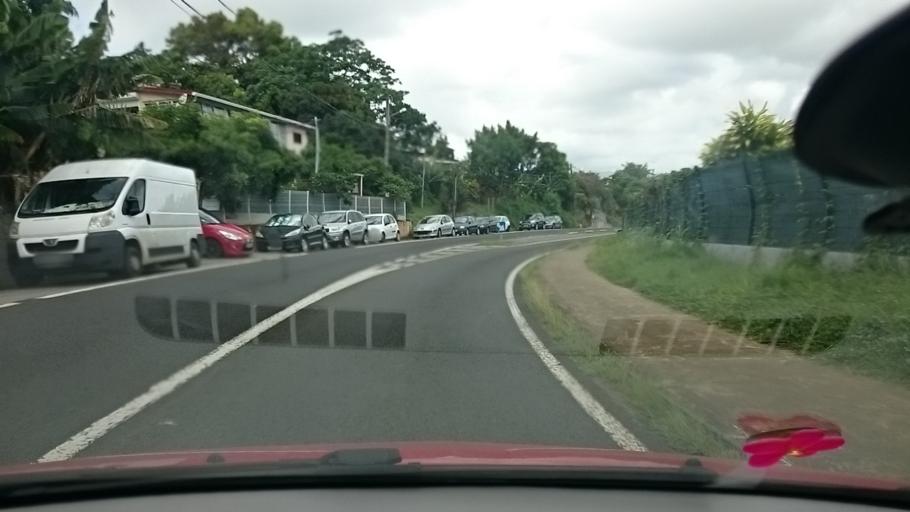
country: MQ
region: Martinique
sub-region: Martinique
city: La Trinite
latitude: 14.7388
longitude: -60.9491
